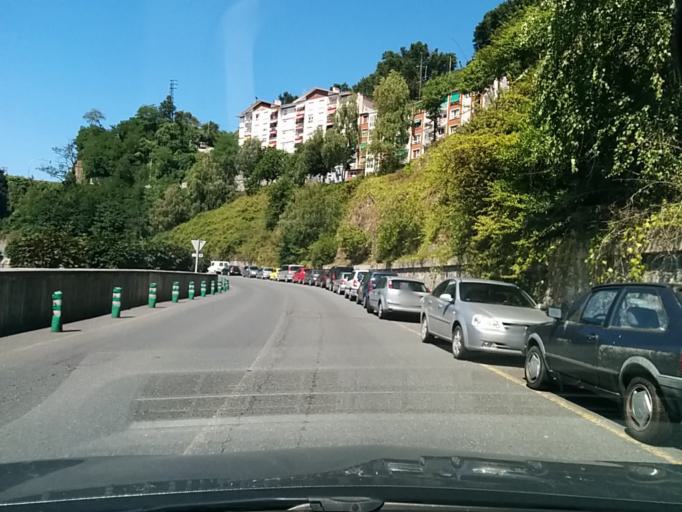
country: ES
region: Basque Country
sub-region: Bizkaia
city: Ondarroa
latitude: 43.3201
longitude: -2.4193
